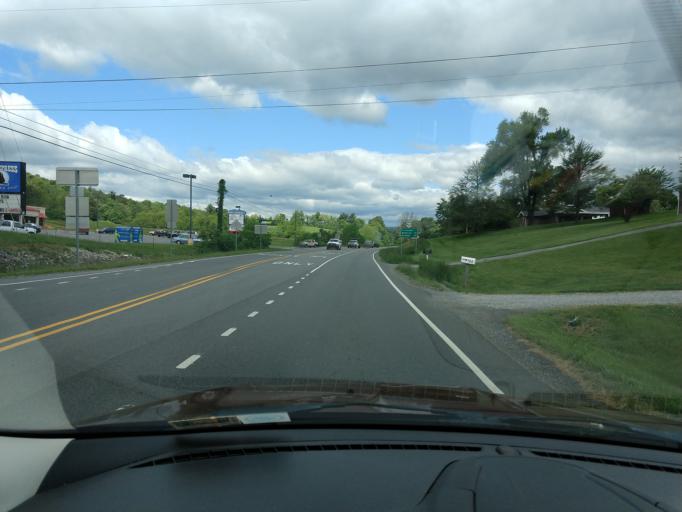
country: US
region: Virginia
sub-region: Wythe County
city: Wytheville
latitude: 36.9304
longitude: -80.9418
